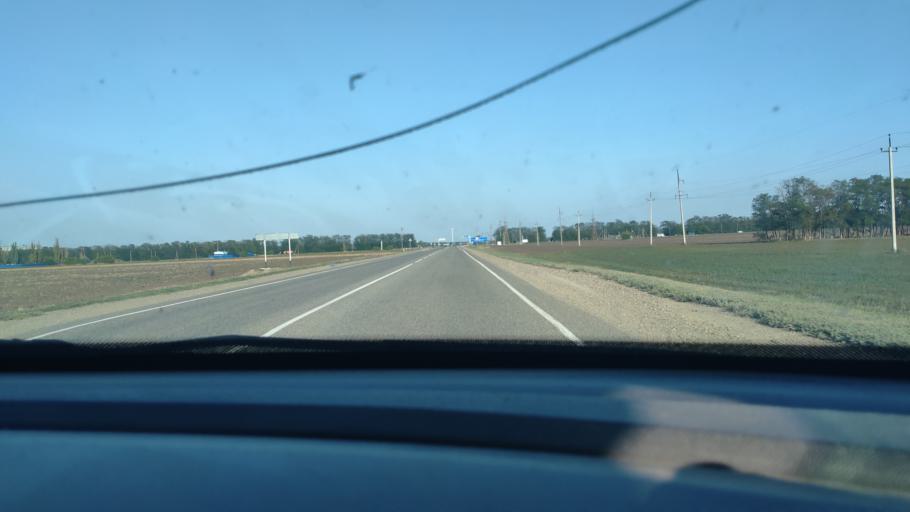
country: RU
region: Krasnodarskiy
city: Staroshcherbinovskaya
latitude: 46.6105
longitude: 38.6471
